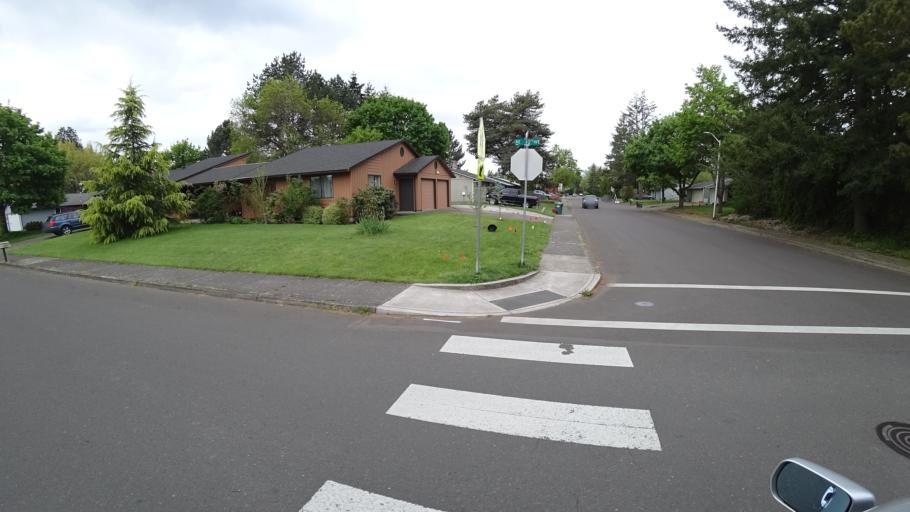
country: US
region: Oregon
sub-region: Washington County
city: Hillsboro
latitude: 45.5350
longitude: -122.9730
